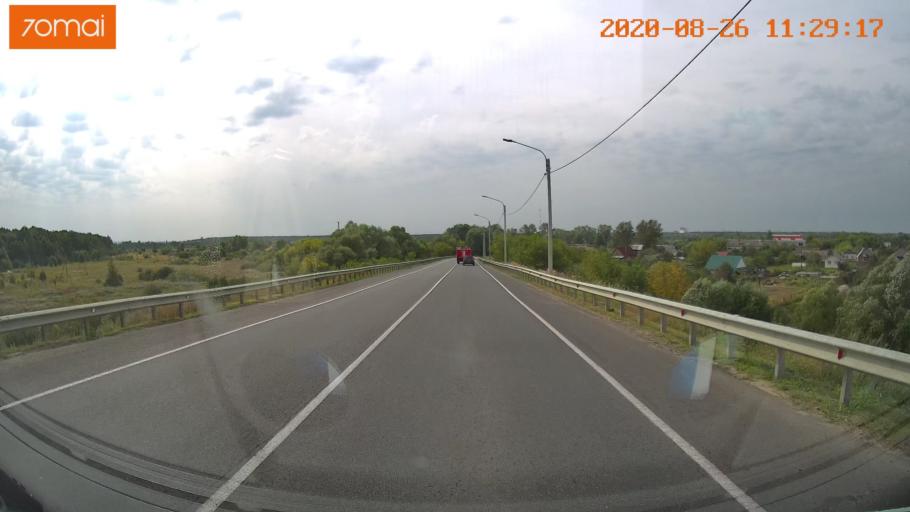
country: RU
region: Rjazan
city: Shilovo
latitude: 54.3211
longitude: 40.9002
